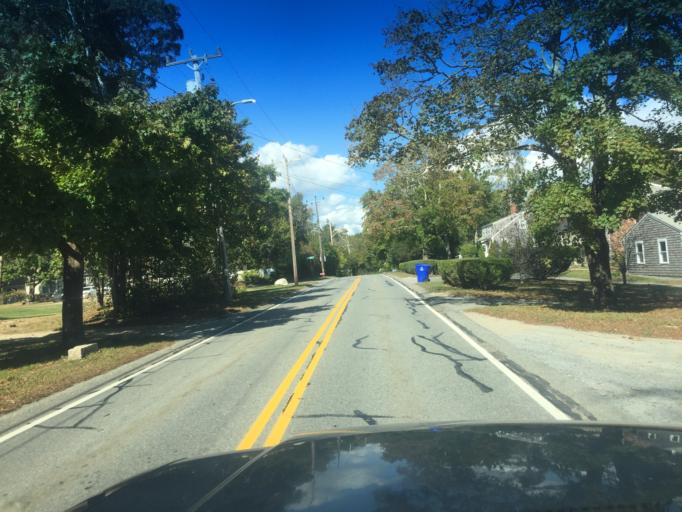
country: US
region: Massachusetts
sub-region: Barnstable County
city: North Falmouth
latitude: 41.6611
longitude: -70.6083
